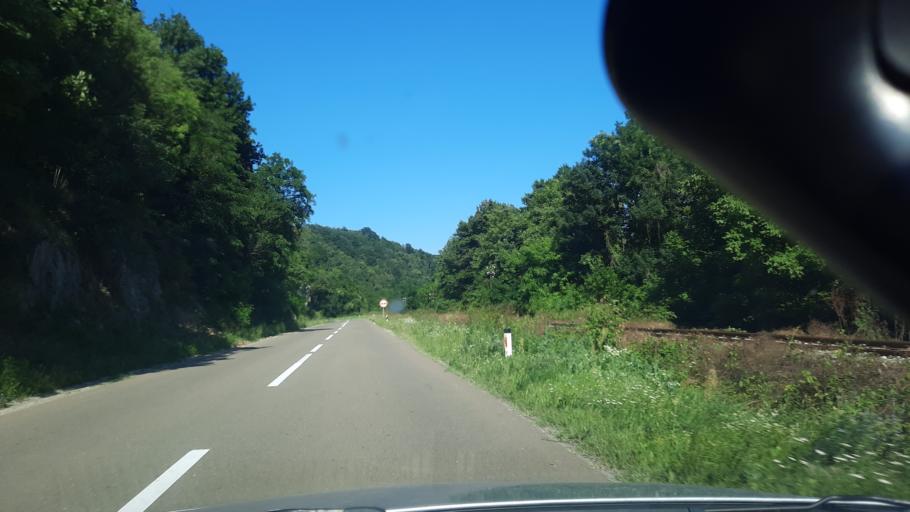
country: RS
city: Turija
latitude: 44.5293
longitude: 21.6239
